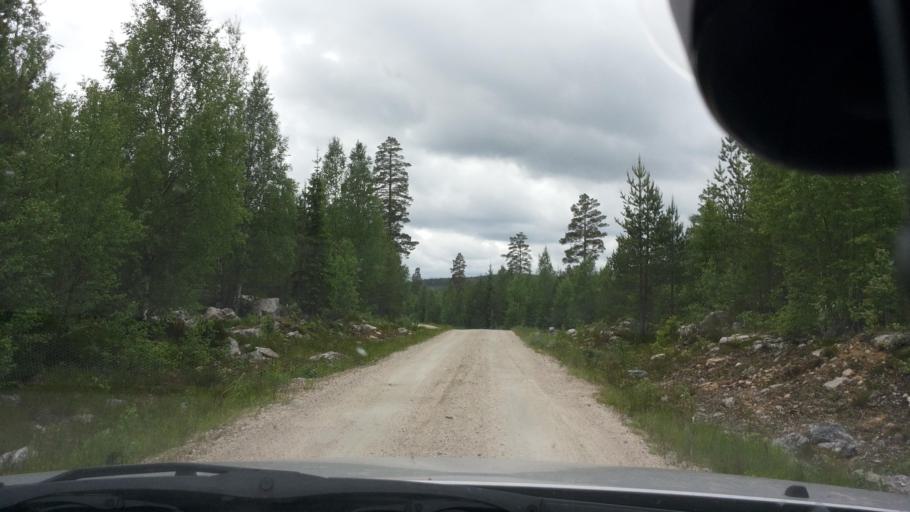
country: SE
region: Gaevleborg
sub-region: Ovanakers Kommun
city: Edsbyn
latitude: 61.4853
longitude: 15.3154
